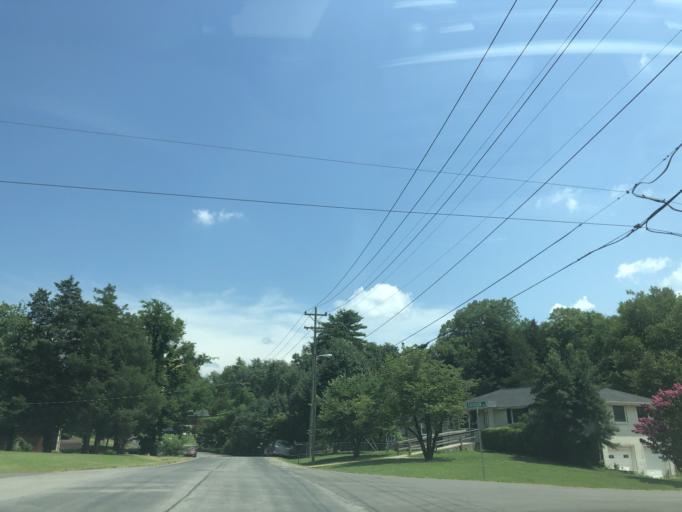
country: US
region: Tennessee
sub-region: Davidson County
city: Lakewood
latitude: 36.1965
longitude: -86.6162
